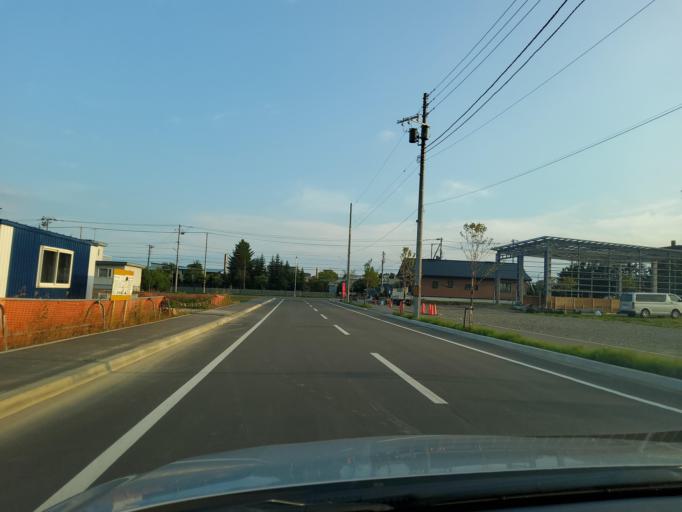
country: JP
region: Hokkaido
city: Obihiro
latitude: 42.9344
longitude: 143.1535
